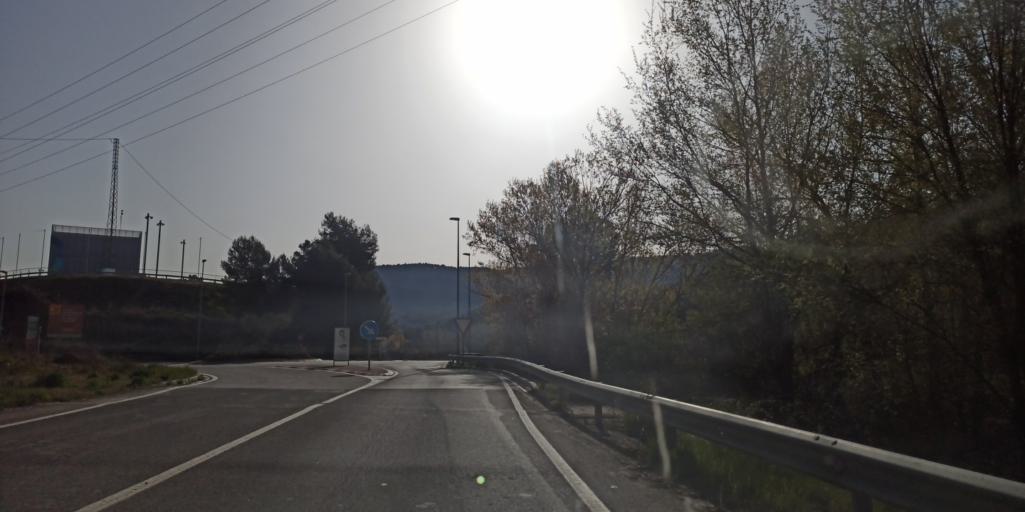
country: ES
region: Catalonia
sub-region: Provincia de Barcelona
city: Castelloli
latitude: 41.5869
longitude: 1.6757
